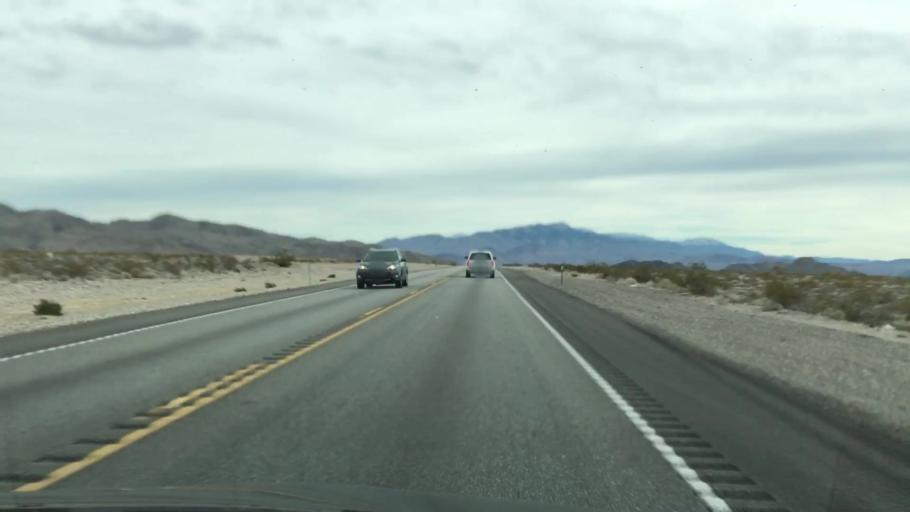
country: US
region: Nevada
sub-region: Nye County
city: Pahrump
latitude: 36.6042
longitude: -116.2560
